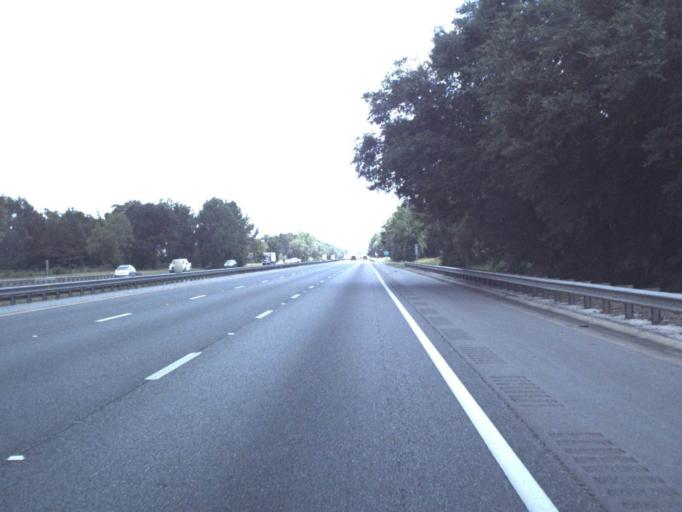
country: US
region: Florida
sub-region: Hamilton County
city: Jasper
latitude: 30.4020
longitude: -82.8863
